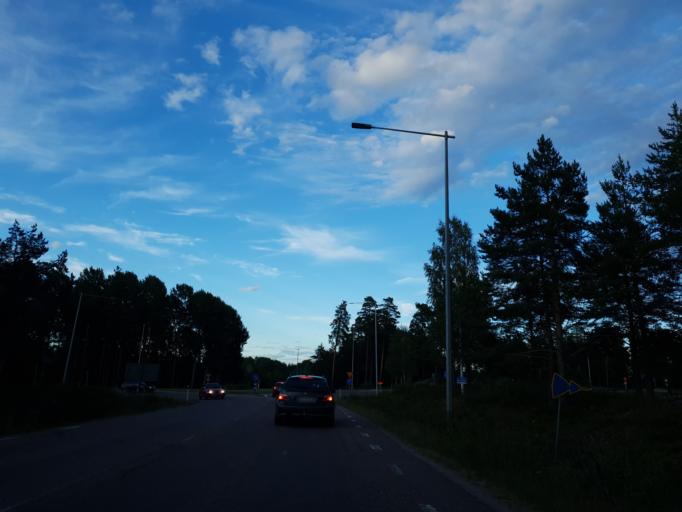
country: SE
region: Gaevleborg
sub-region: Soderhamns Kommun
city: Soderhamn
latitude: 61.2916
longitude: 17.0701
